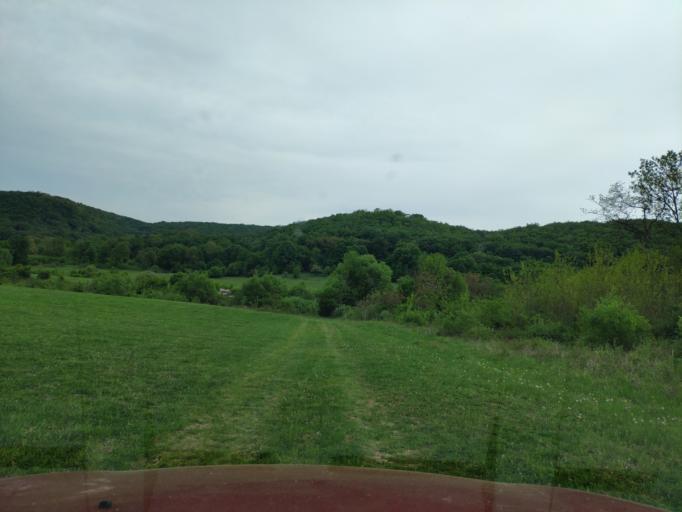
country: SK
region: Banskobystricky
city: Revuca
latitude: 48.5187
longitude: 20.1315
